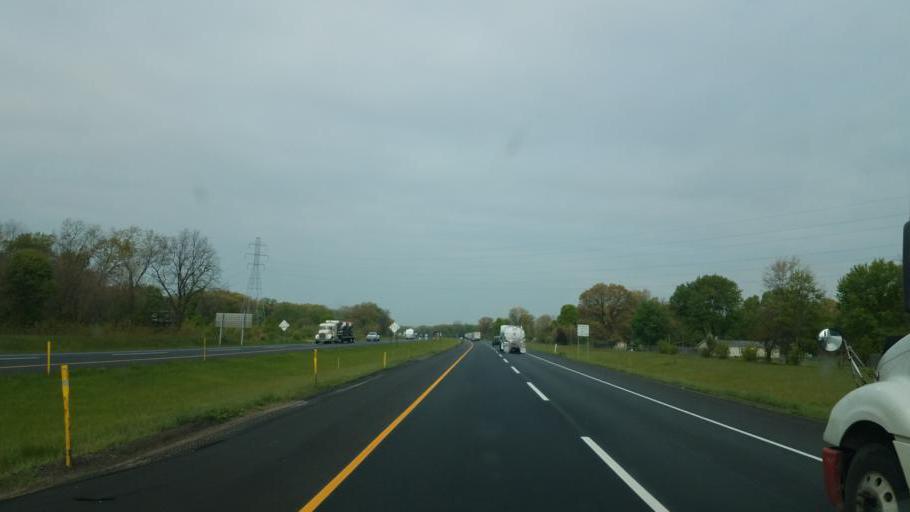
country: US
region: Indiana
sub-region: Elkhart County
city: Simonton Lake
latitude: 41.7327
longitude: -86.0217
